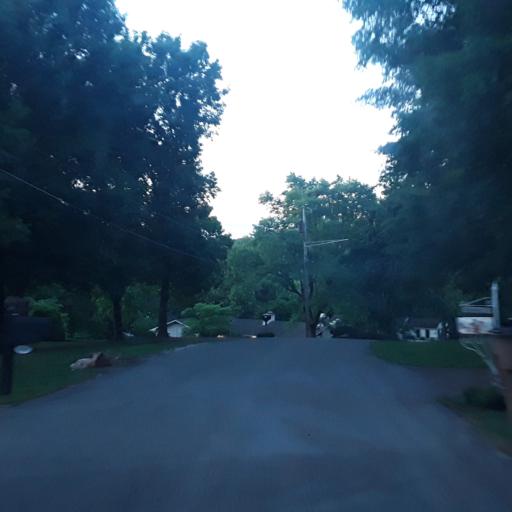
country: US
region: Tennessee
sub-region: Davidson County
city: Oak Hill
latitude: 36.0680
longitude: -86.7614
